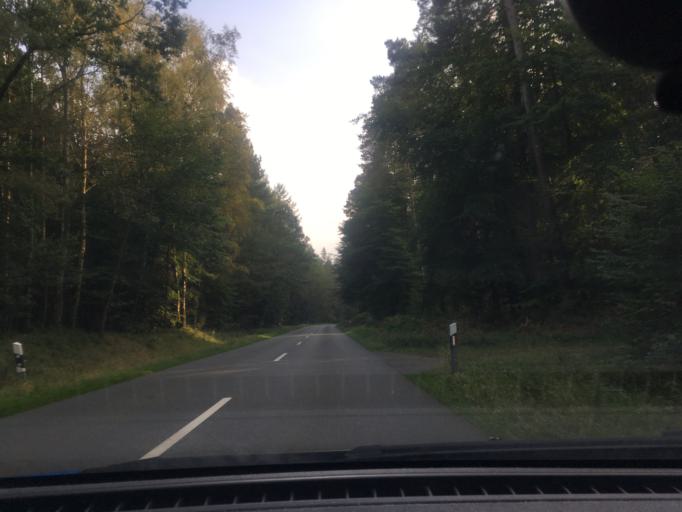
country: DE
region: Lower Saxony
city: Barendorf
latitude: 53.2482
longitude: 10.5289
